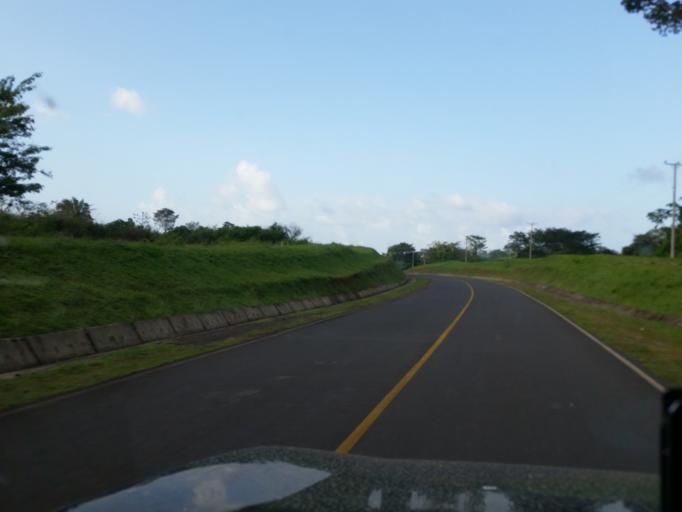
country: NI
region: Rio San Juan
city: San Carlos
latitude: 11.1841
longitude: -84.6779
